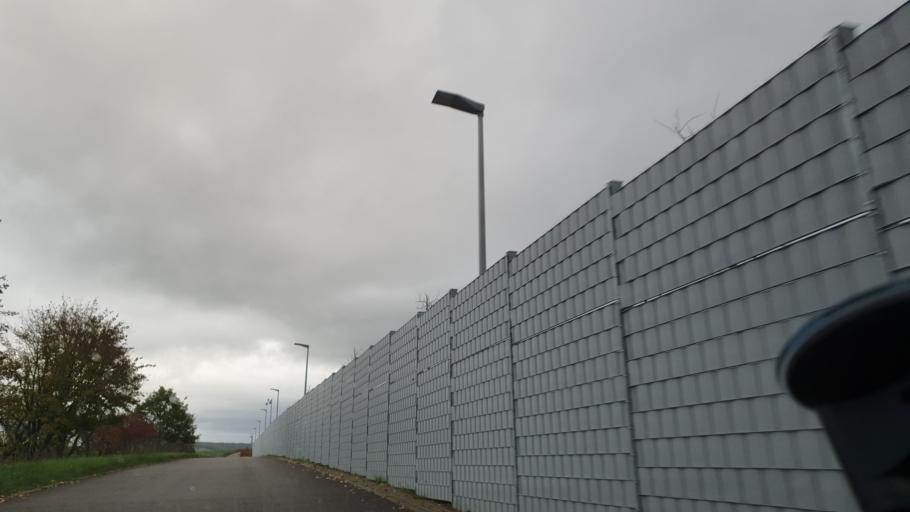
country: DE
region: Baden-Wuerttemberg
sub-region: Regierungsbezirk Stuttgart
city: Abstatt
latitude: 49.0795
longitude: 9.3029
